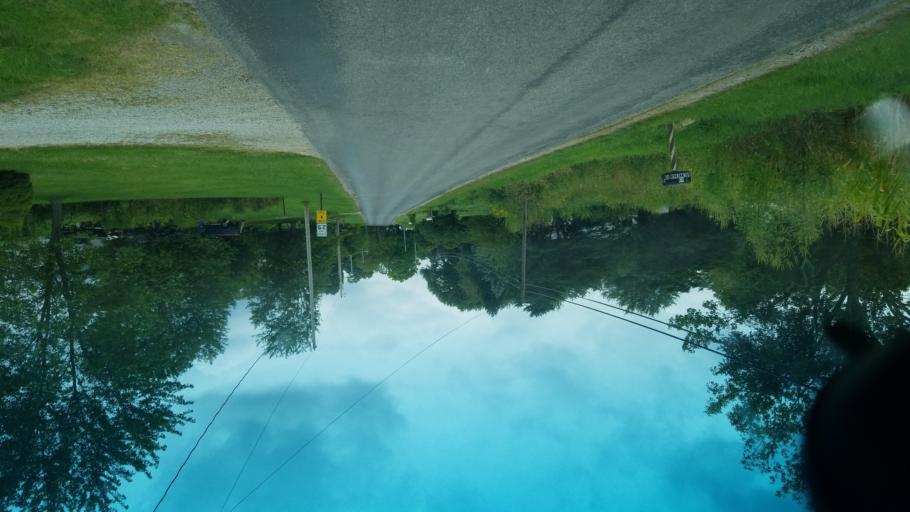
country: US
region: Ohio
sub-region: Huron County
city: Plymouth
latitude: 40.9717
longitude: -82.5939
